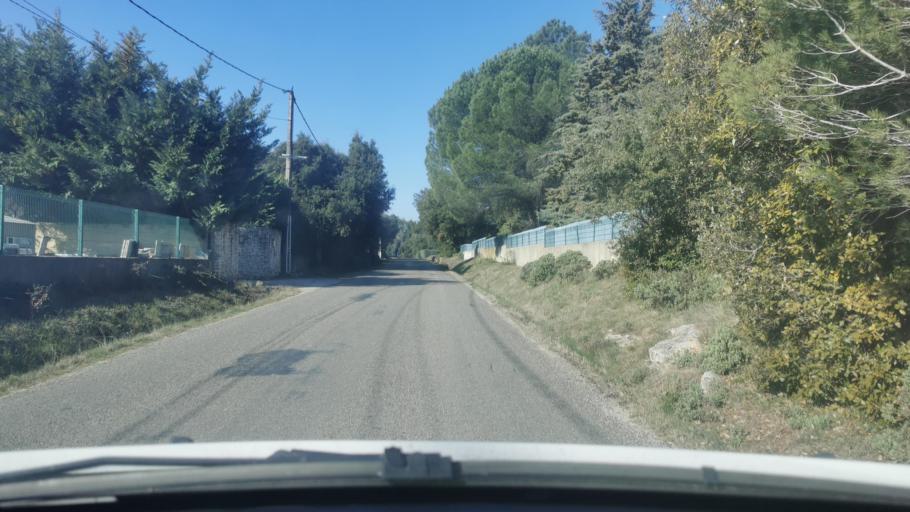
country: FR
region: Languedoc-Roussillon
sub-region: Departement du Gard
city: Montaren-et-Saint-Mediers
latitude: 44.0457
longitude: 4.3974
